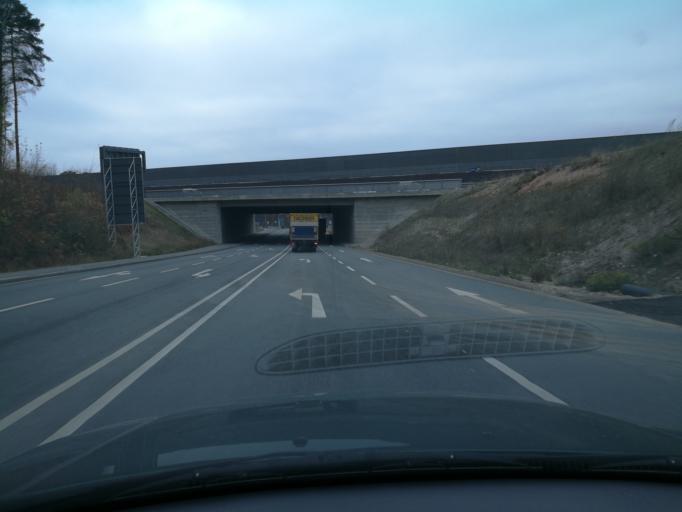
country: DE
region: Bavaria
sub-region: Regierungsbezirk Mittelfranken
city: Wendelstein
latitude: 49.3906
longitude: 11.1709
